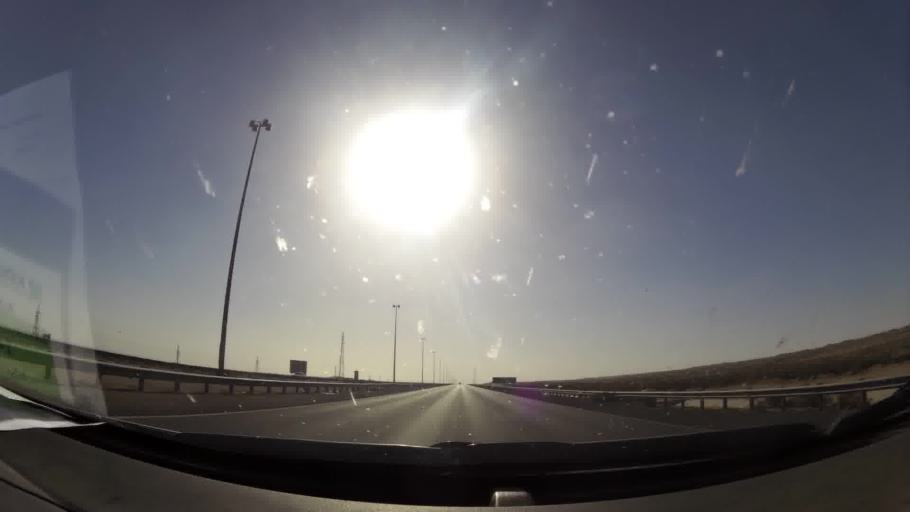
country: KW
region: Al Asimah
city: Kuwait City
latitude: 29.5660
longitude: 47.8918
